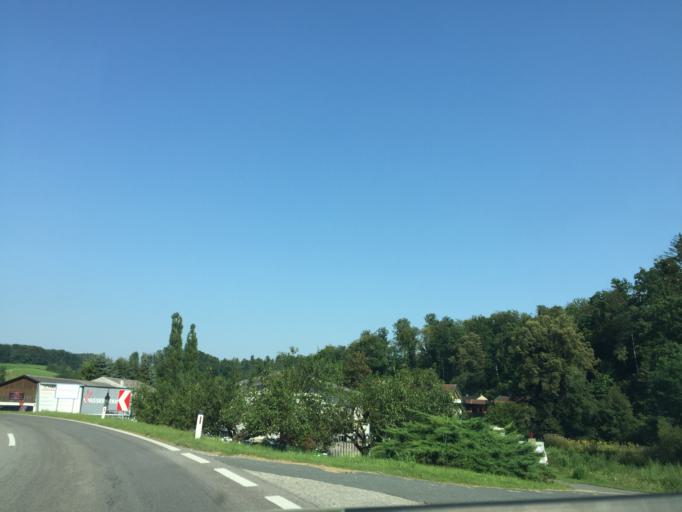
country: AT
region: Styria
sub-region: Politischer Bezirk Leibnitz
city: Ehrenhausen
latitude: 46.7189
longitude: 15.5829
